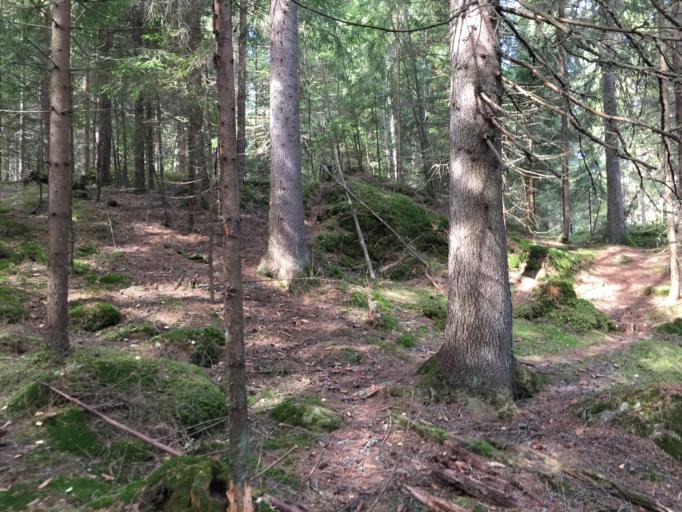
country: NO
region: Akershus
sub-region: Skedsmo
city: Lillestrom
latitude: 59.9282
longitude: 11.0284
